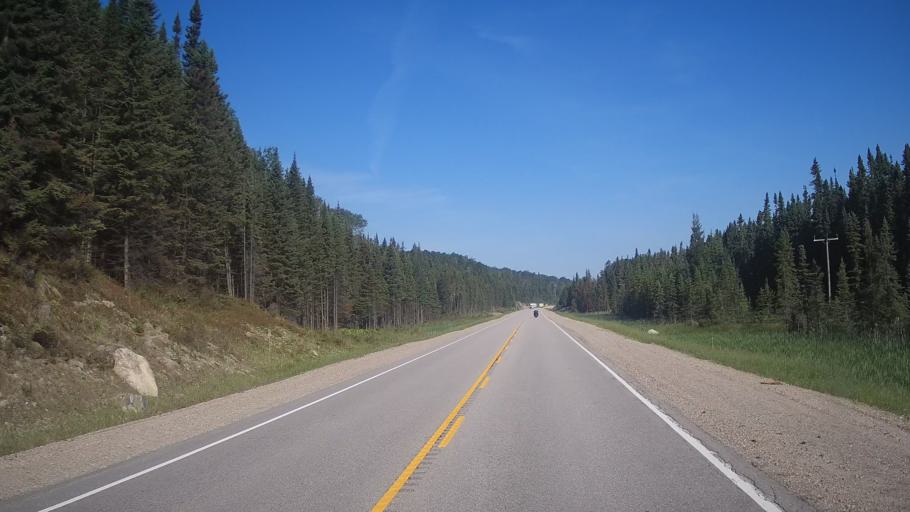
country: CA
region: Ontario
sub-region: Rainy River District
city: Atikokan
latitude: 49.4758
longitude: -91.9430
